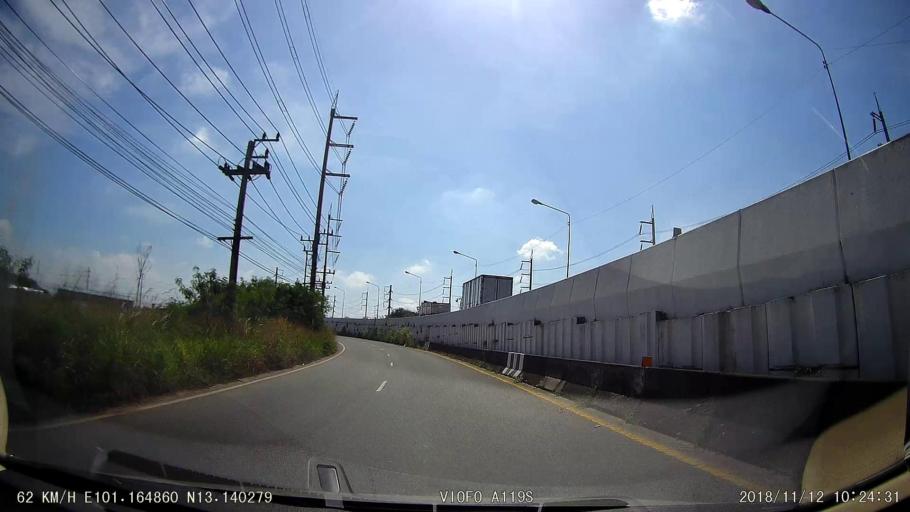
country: TH
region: Chon Buri
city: Ban Talat Bueng
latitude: 13.1401
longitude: 101.1650
